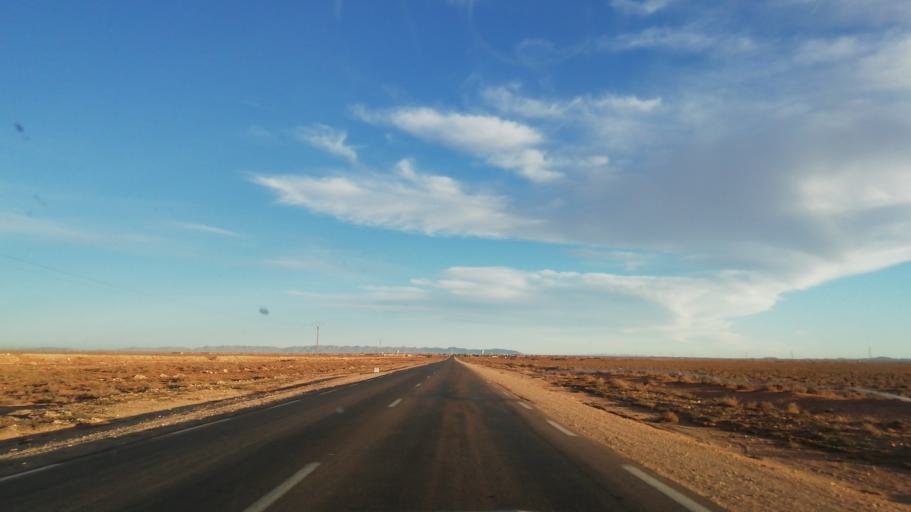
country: DZ
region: Wilaya de Naama
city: Naama
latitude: 33.7334
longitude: -0.7581
